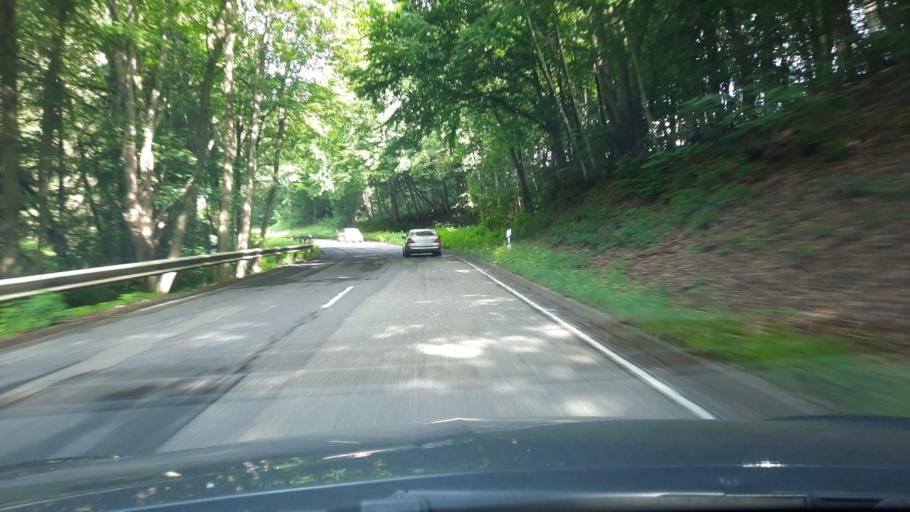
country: DE
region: Rheinland-Pfalz
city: Spessart
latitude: 50.4458
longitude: 7.1297
